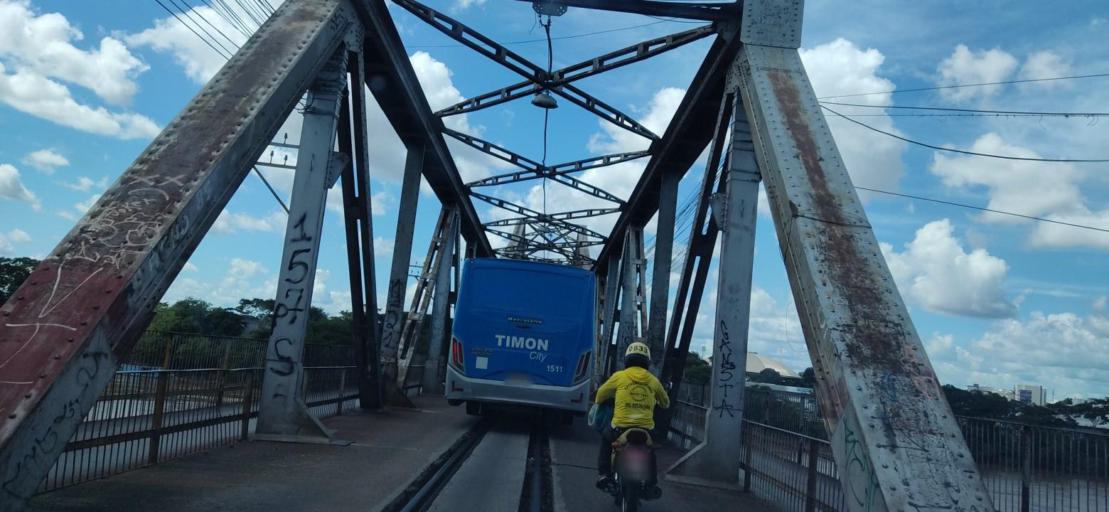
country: BR
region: Maranhao
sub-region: Timon
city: Timon
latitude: -5.0873
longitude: -42.8251
